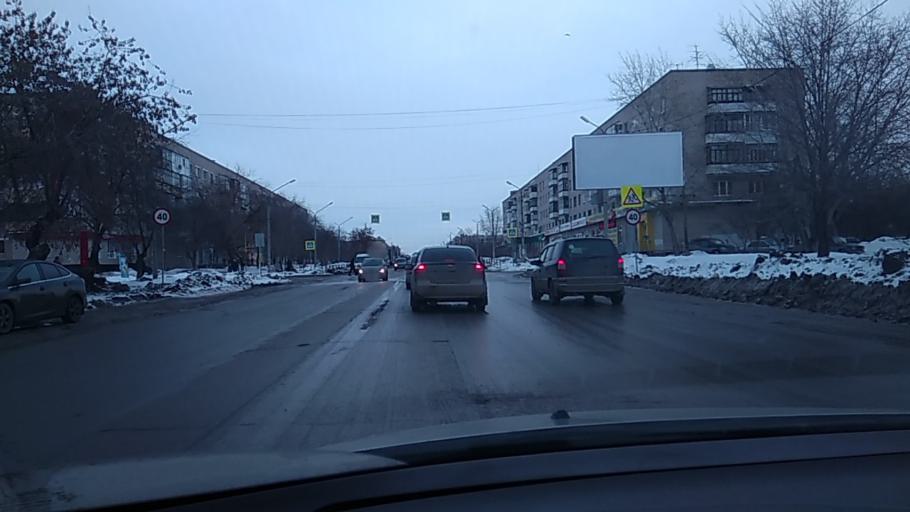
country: RU
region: Sverdlovsk
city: Kamensk-Ural'skiy
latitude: 56.4207
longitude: 61.9127
